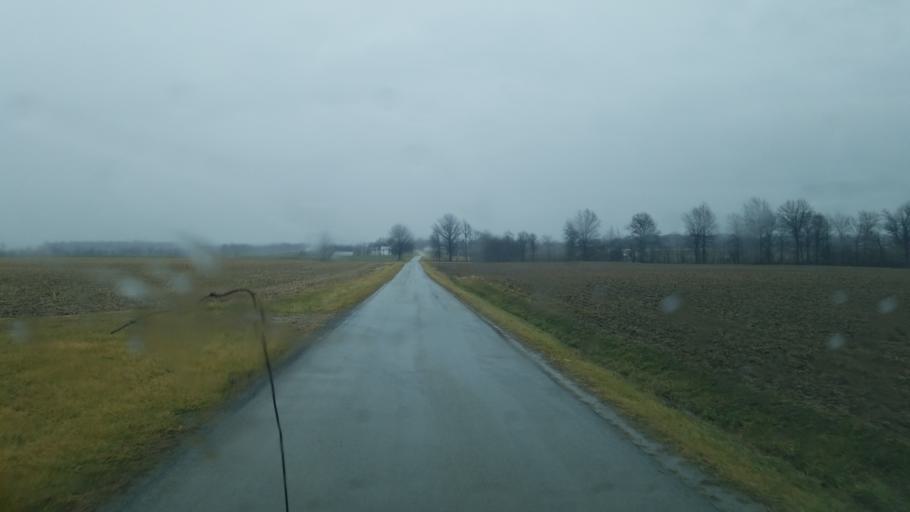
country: US
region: Ohio
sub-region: Hardin County
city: Forest
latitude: 40.7595
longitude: -83.3985
